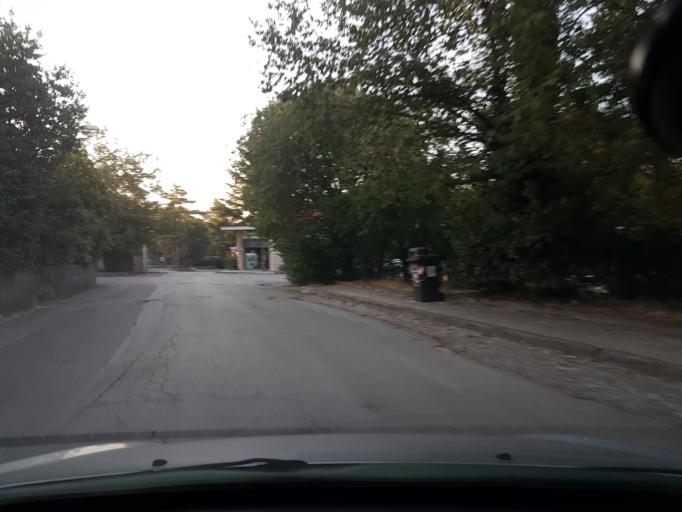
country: IT
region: Friuli Venezia Giulia
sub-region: Provincia di Trieste
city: Santa Croce
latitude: 45.7364
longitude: 13.6909
